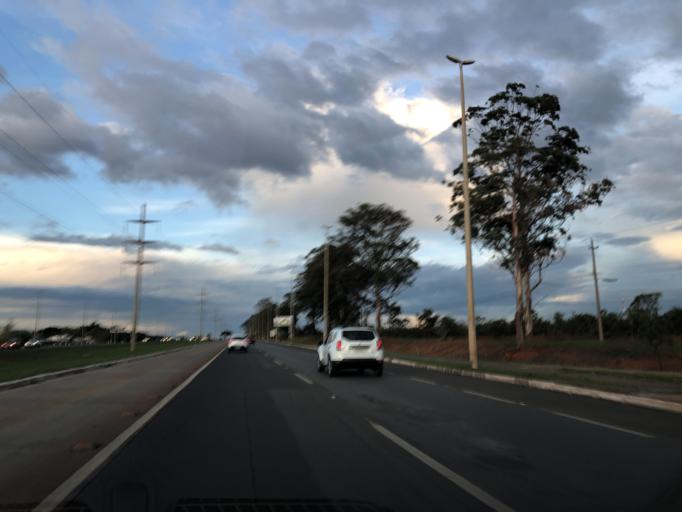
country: BR
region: Federal District
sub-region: Brasilia
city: Brasilia
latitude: -15.9805
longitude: -48.0360
